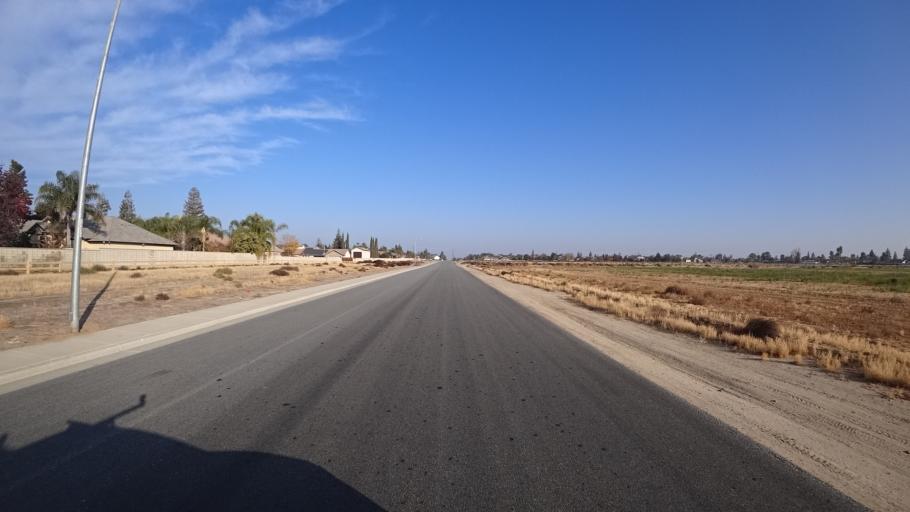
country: US
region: California
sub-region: Kern County
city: Rosedale
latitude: 35.3729
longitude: -119.1722
